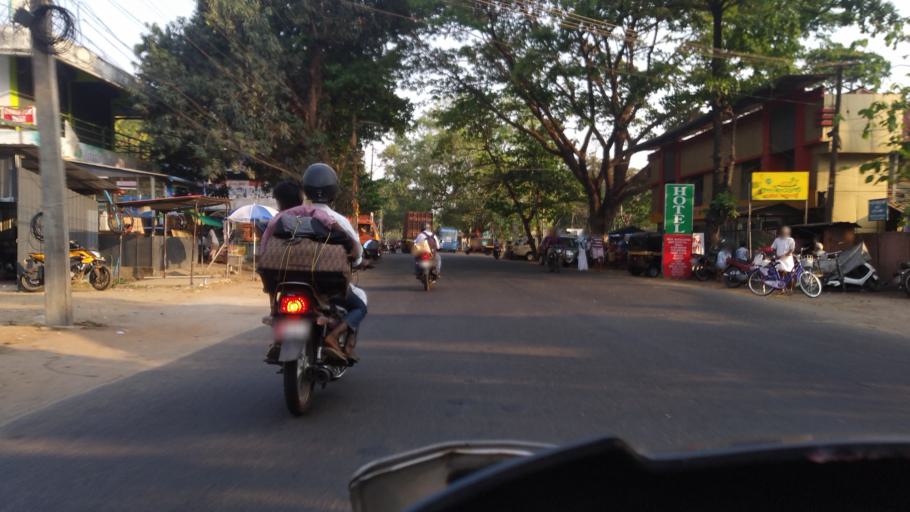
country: IN
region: Kerala
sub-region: Thrissur District
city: Thanniyam
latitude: 10.3955
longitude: 76.1161
